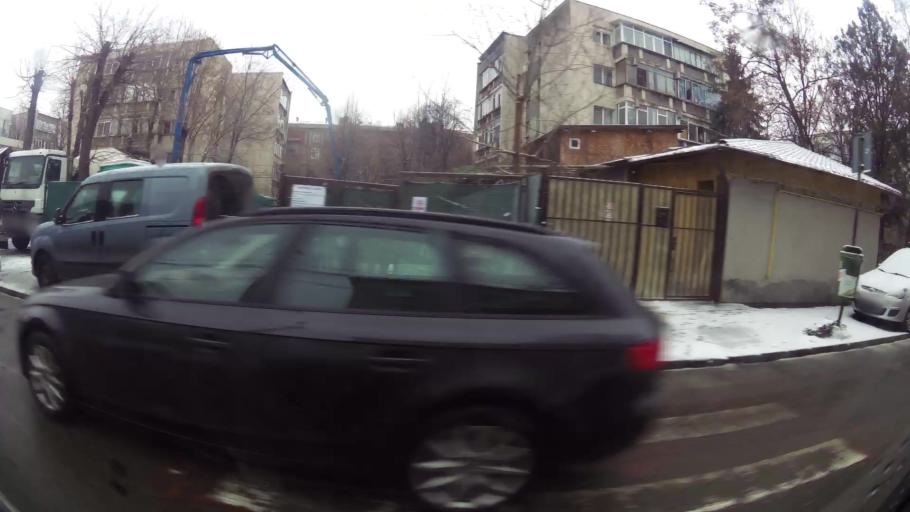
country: RO
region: Prahova
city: Ploiesti
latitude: 44.9275
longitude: 26.0246
